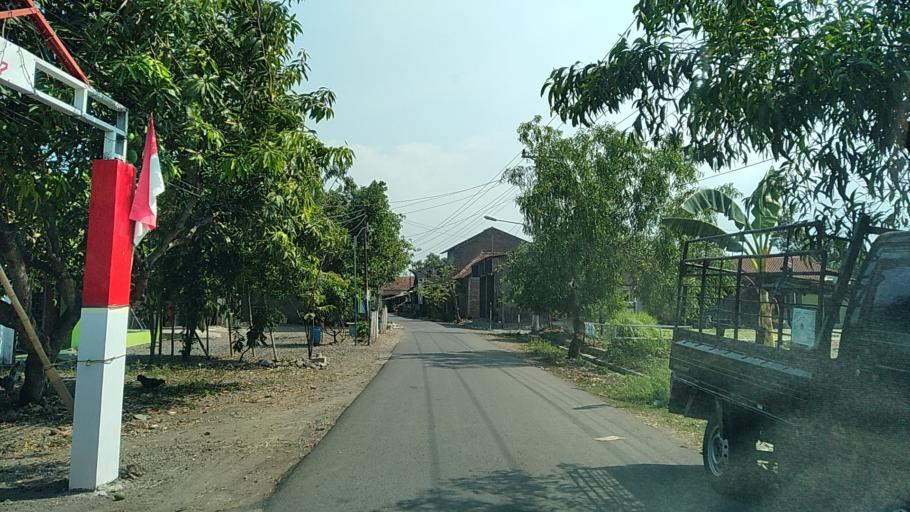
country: ID
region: Central Java
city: Mranggen
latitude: -7.0517
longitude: 110.4801
